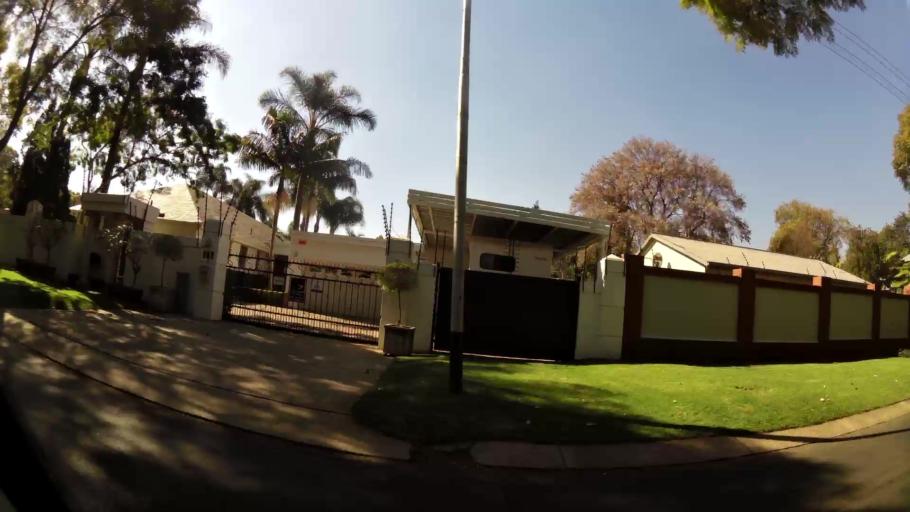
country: ZA
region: Gauteng
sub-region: City of Tshwane Metropolitan Municipality
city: Pretoria
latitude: -25.7755
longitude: 28.2439
